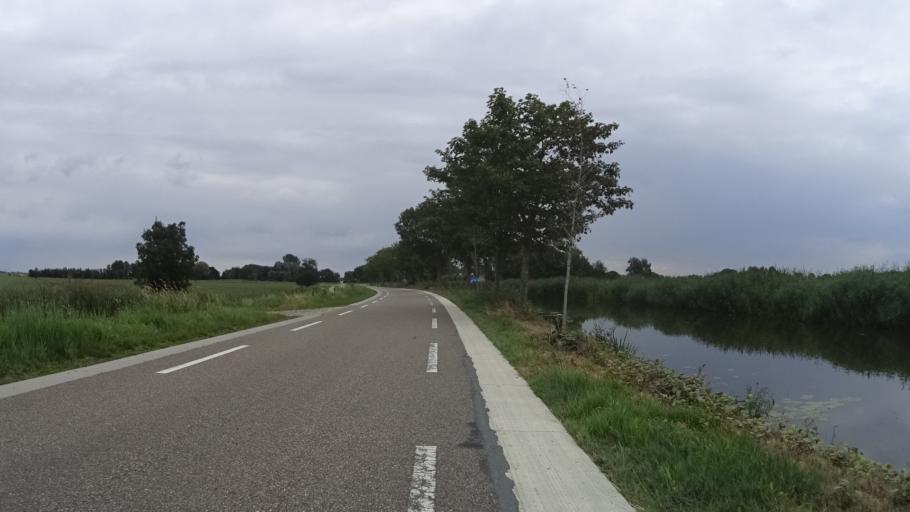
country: NL
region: Groningen
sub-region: Gemeente Slochteren
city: Slochteren
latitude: 53.2352
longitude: 6.7320
